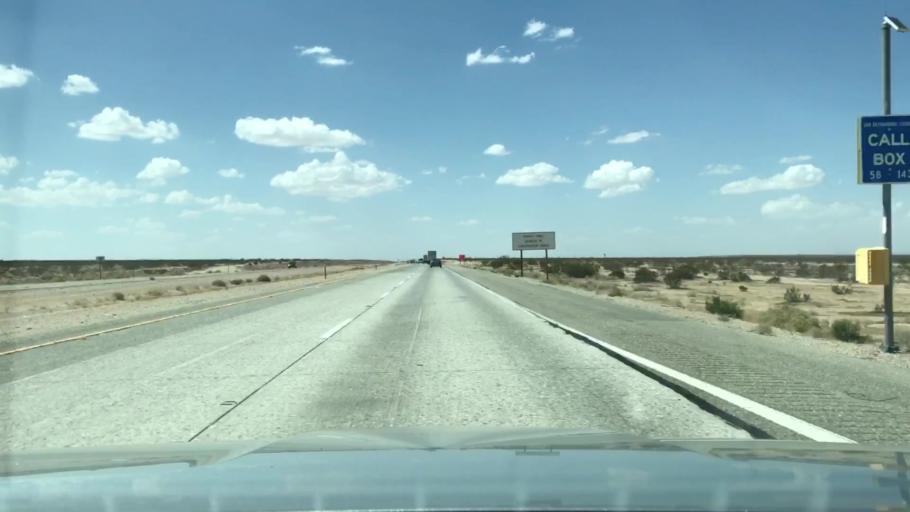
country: US
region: California
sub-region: Kern County
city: Boron
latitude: 34.9443
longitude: -117.4019
